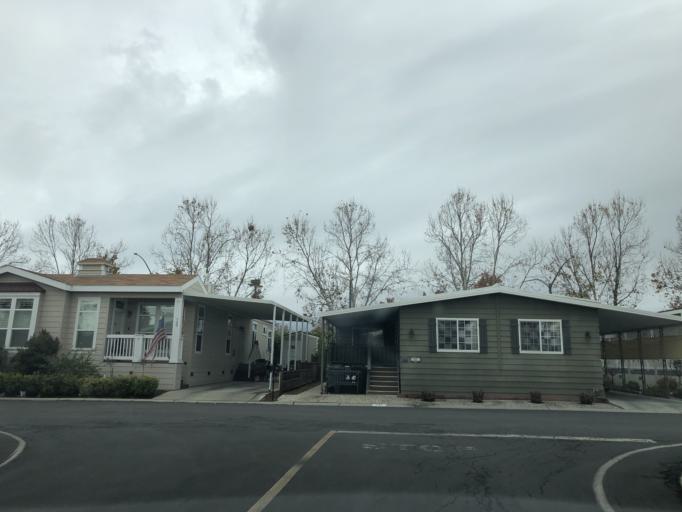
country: US
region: California
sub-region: Santa Clara County
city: Sunnyvale
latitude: 37.4029
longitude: -121.9977
